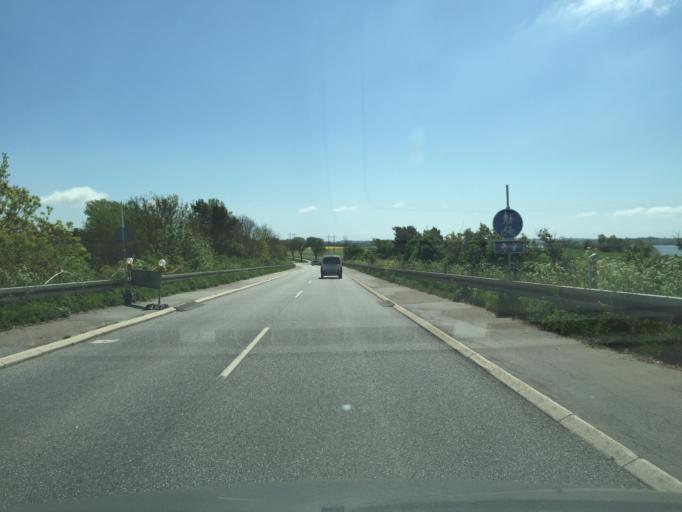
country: DK
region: Zealand
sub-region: Vordingborg Kommune
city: Stege
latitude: 54.9857
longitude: 12.1687
